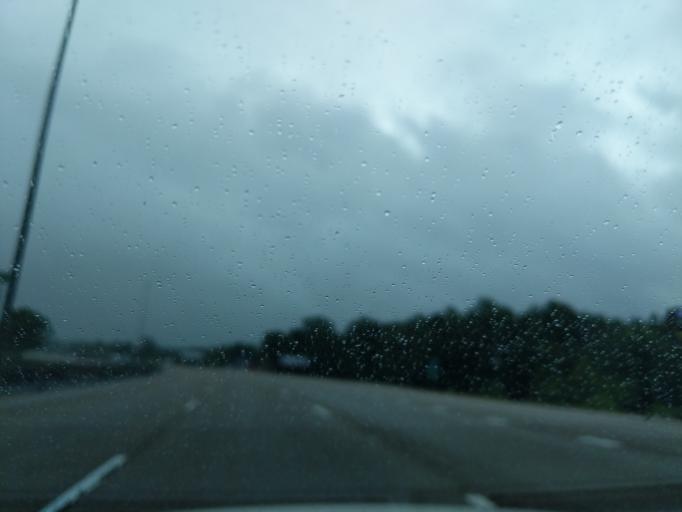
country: US
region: Mississippi
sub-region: Rankin County
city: Pearl
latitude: 32.2659
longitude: -90.1448
